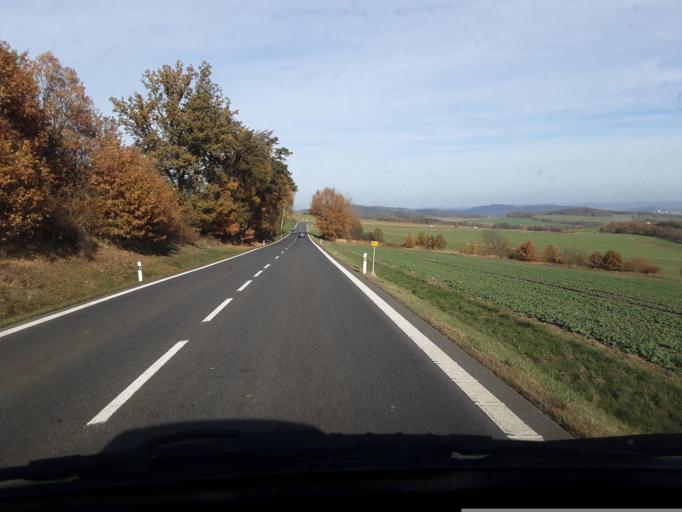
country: CZ
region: Plzensky
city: Janovice nad Uhlavou
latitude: 49.3772
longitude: 13.1761
